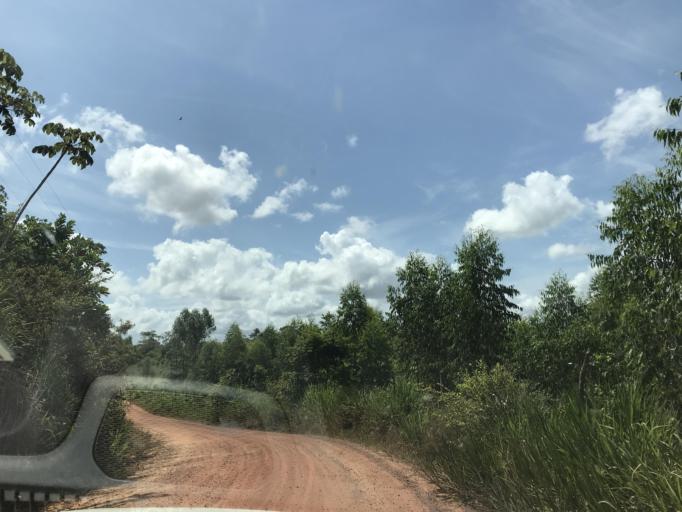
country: BR
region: Bahia
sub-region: Entre Rios
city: Entre Rios
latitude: -12.2171
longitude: -38.0776
